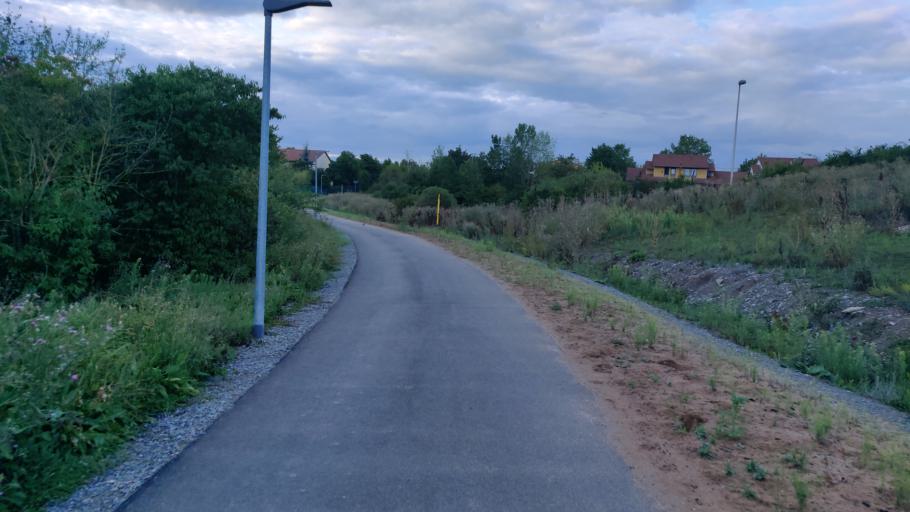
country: DE
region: Bavaria
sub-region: Regierungsbezirk Unterfranken
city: Niederwerrn
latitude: 50.0578
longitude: 10.1988
